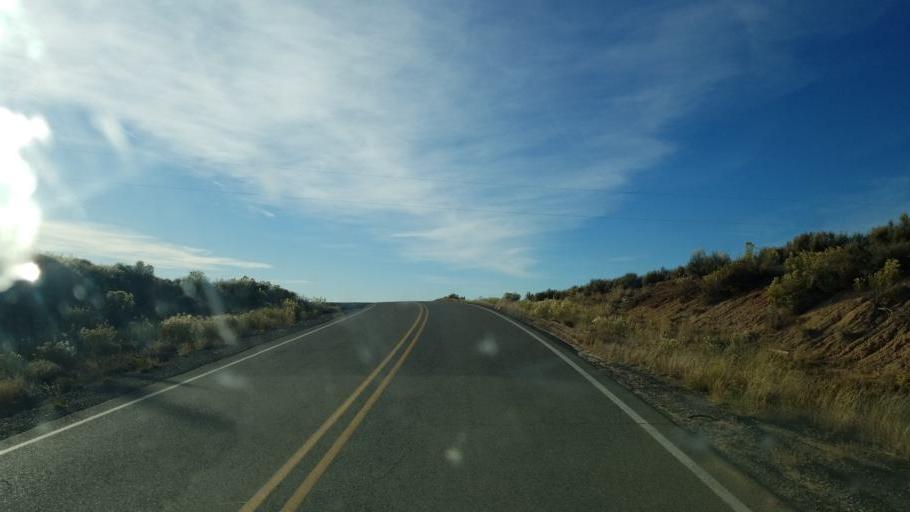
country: US
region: New Mexico
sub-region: San Juan County
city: Bloomfield
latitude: 36.7321
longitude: -107.6827
